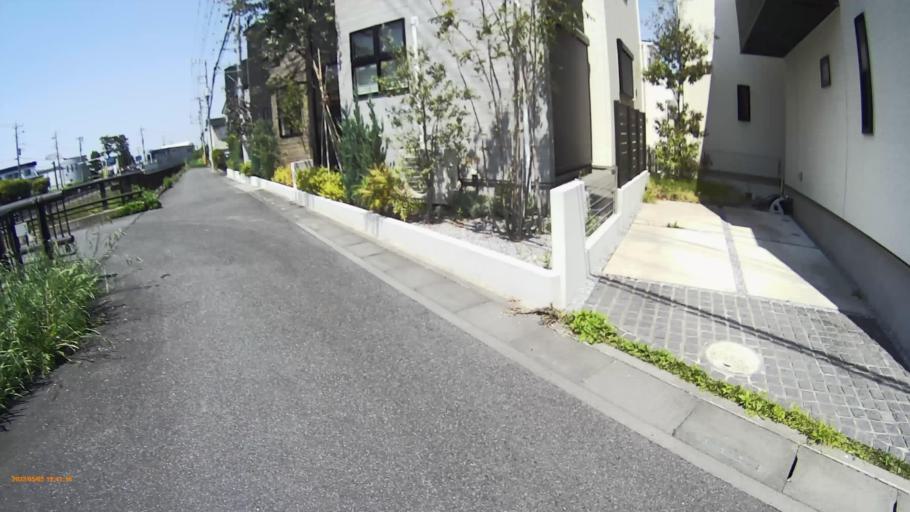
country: JP
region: Saitama
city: Kasukabe
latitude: 35.9434
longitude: 139.7764
